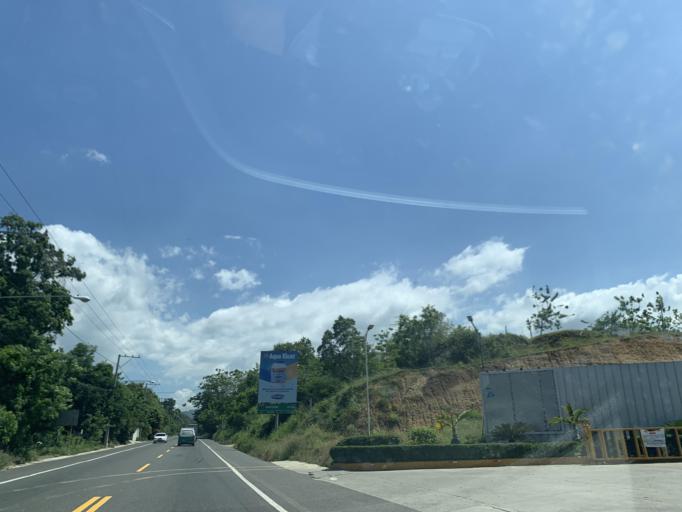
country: DO
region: Puerto Plata
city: Imbert
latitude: 19.7166
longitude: -70.8342
